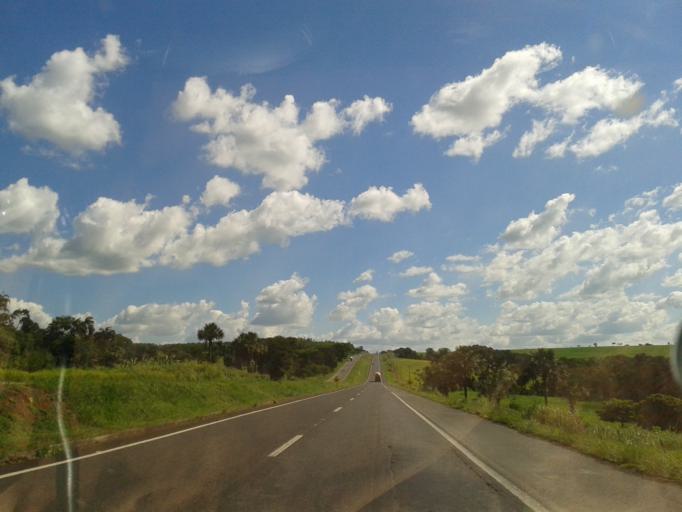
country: BR
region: Goias
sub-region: Morrinhos
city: Morrinhos
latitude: -17.7317
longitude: -49.1554
